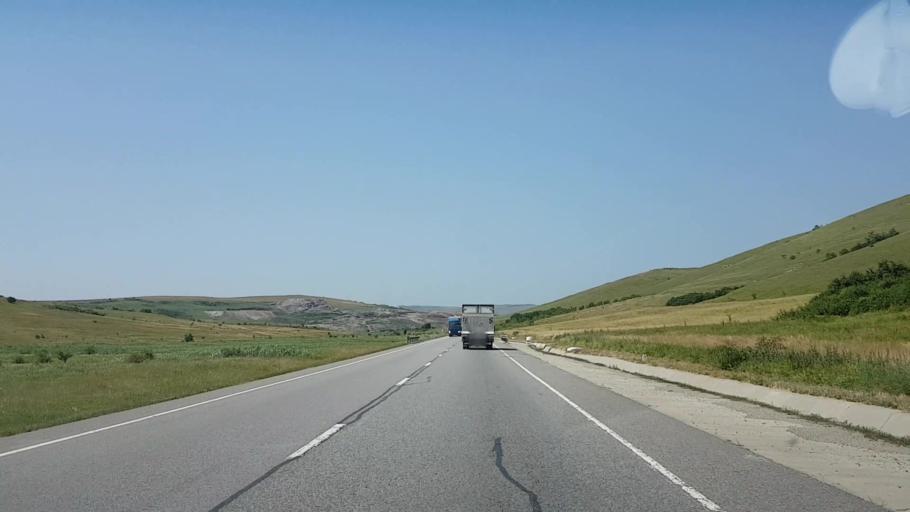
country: RO
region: Cluj
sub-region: Comuna Apahida
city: Dezmir
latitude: 46.7532
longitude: 23.7023
